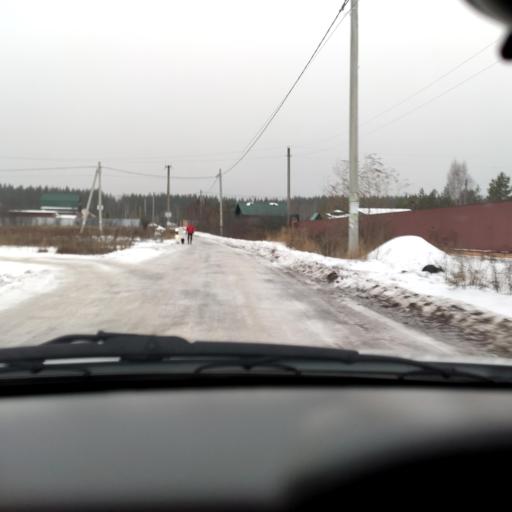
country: RU
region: Voronezj
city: Ramon'
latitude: 51.8863
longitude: 39.2634
